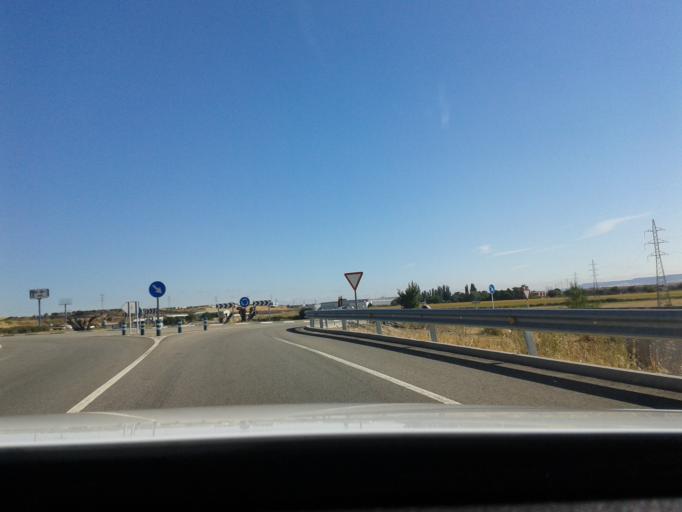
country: ES
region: Castille-La Mancha
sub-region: Provincia de Guadalajara
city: Alovera
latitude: 40.5977
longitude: -3.2582
